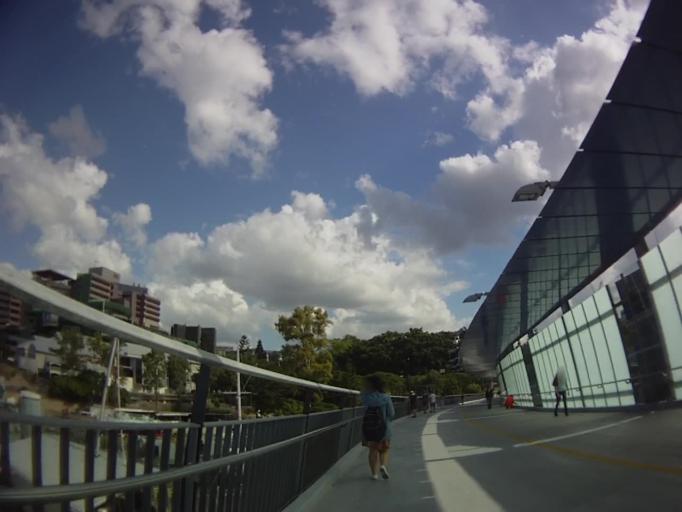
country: AU
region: Queensland
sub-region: Brisbane
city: South Brisbane
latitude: -27.4813
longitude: 153.0266
